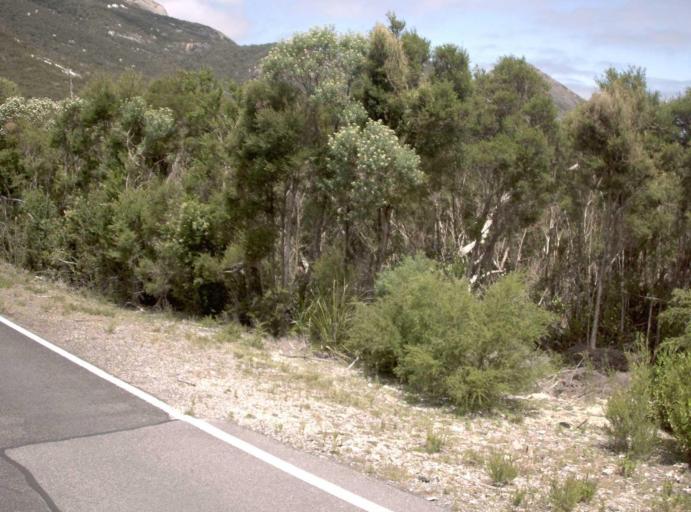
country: AU
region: Victoria
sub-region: Latrobe
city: Morwell
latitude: -39.0255
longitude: 146.3318
